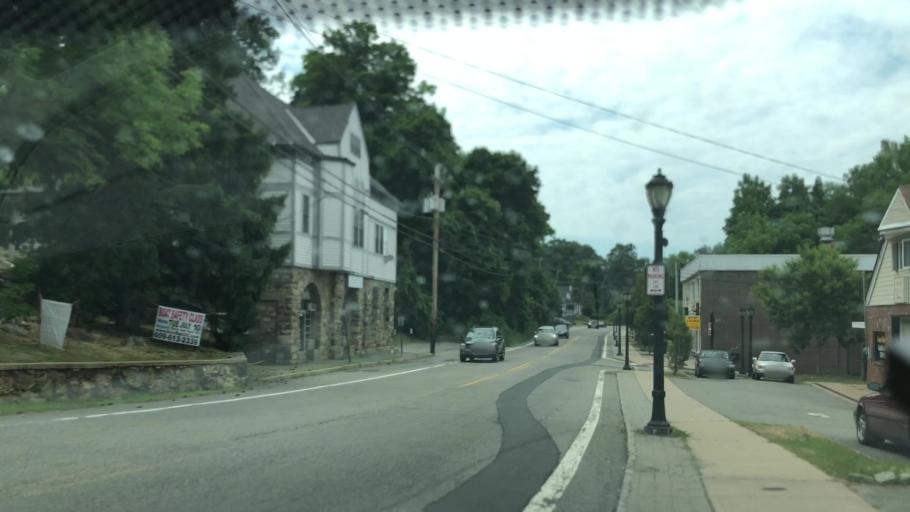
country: US
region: New Jersey
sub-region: Morris County
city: Mount Arlington
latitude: 40.9297
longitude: -74.6327
